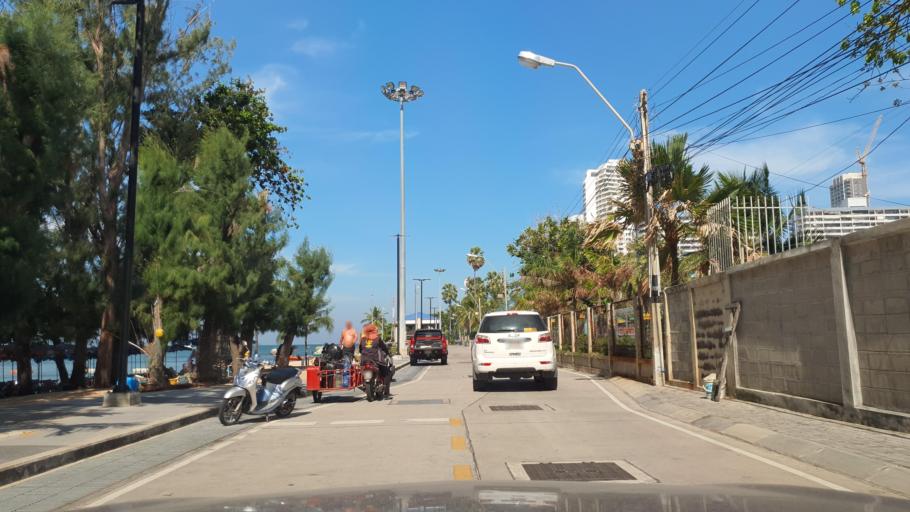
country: TH
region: Chon Buri
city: Phatthaya
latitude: 12.9043
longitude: 100.8613
